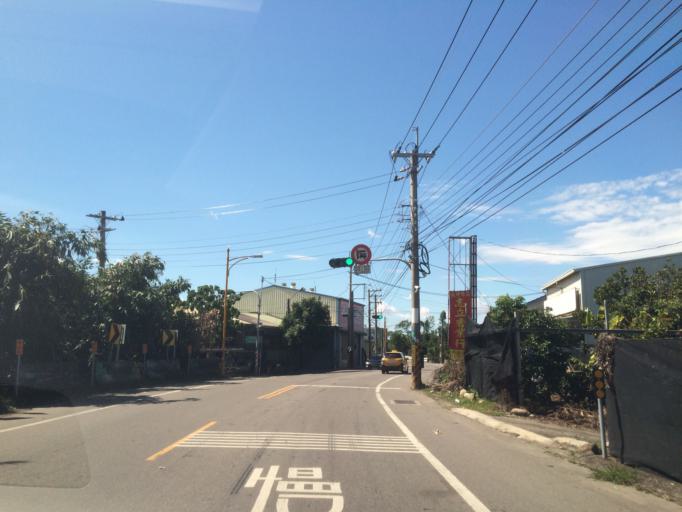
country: TW
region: Taiwan
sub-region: Yunlin
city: Douliu
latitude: 23.7029
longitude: 120.5709
